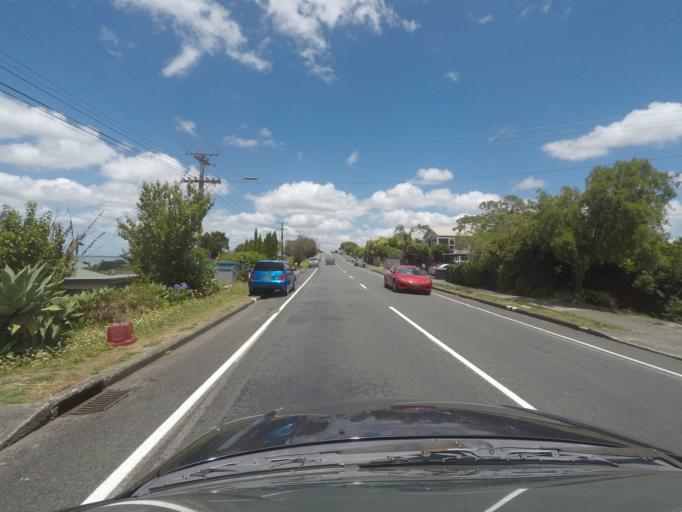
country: NZ
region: Northland
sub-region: Whangarei
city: Whangarei
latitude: -35.7619
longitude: 174.3671
